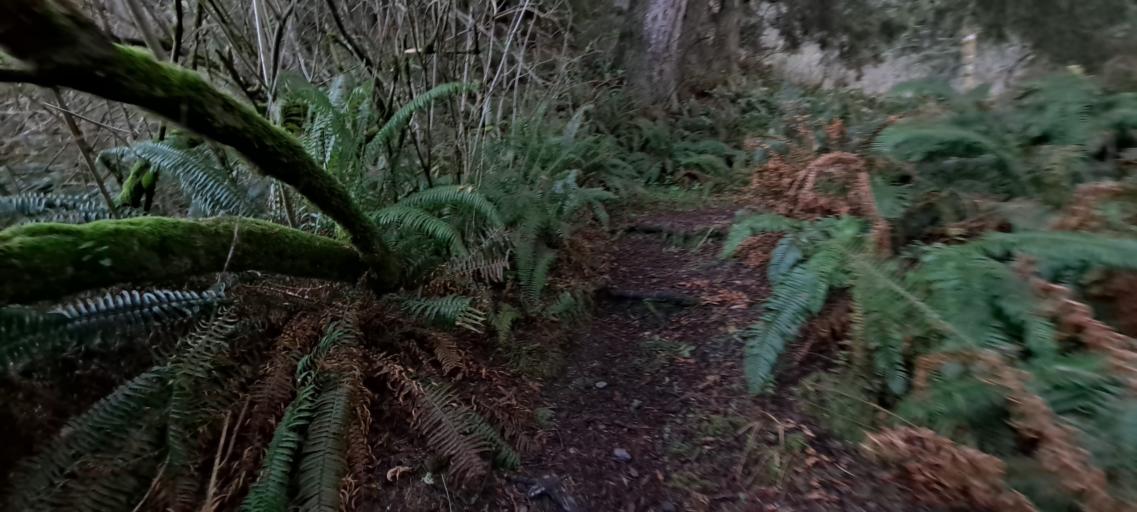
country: US
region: California
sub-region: Humboldt County
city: Ferndale
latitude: 40.5719
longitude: -124.2580
